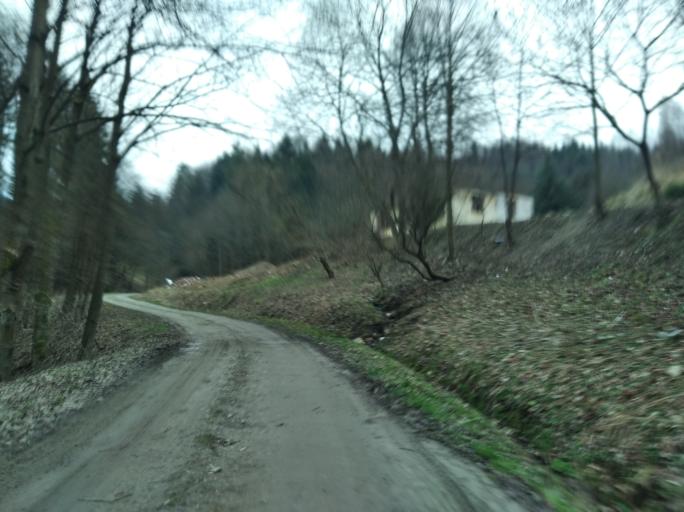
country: PL
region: Subcarpathian Voivodeship
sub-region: Powiat strzyzowski
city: Strzyzow
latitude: 49.8551
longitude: 21.8319
